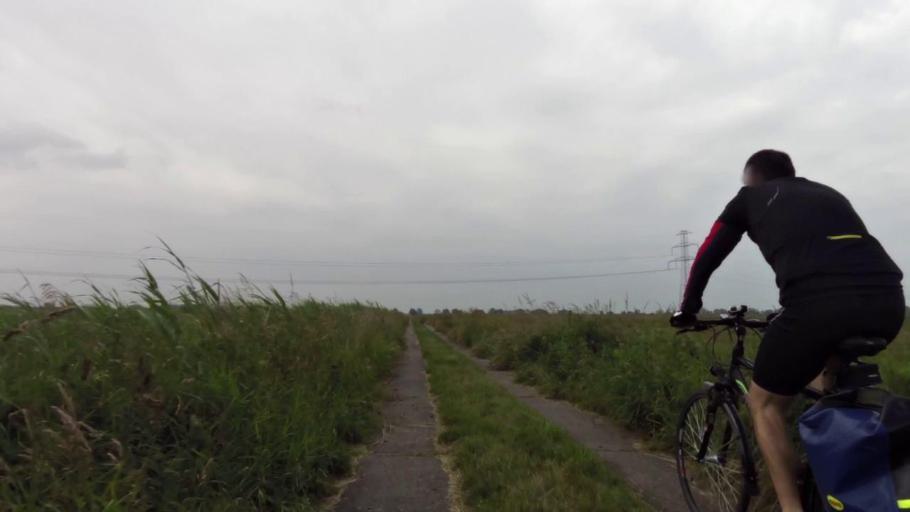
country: PL
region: West Pomeranian Voivodeship
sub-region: Powiat goleniowski
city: Stepnica
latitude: 53.5634
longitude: 14.6985
